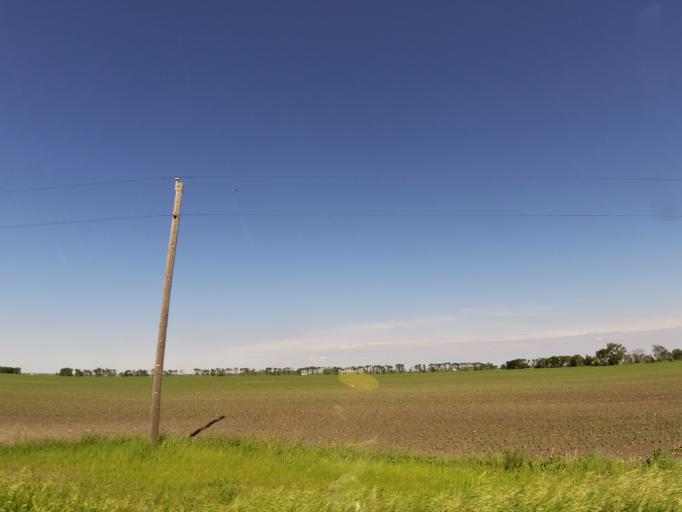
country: US
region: North Dakota
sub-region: Walsh County
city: Grafton
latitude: 48.3481
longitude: -97.2329
